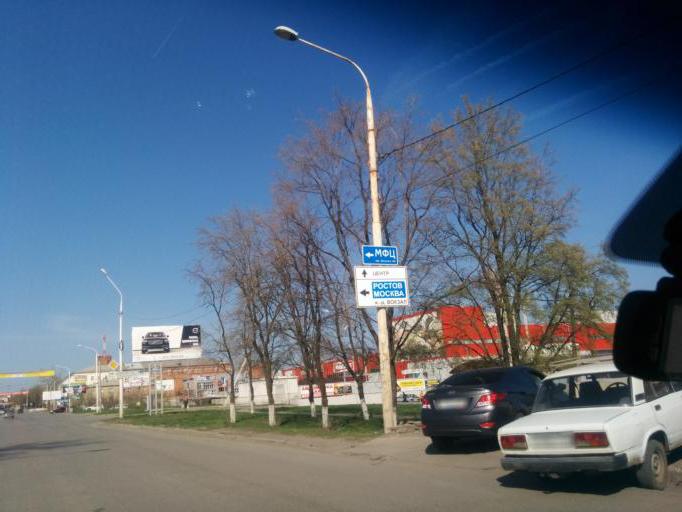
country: RU
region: Rostov
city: Shakhty
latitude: 47.6969
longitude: 40.2074
